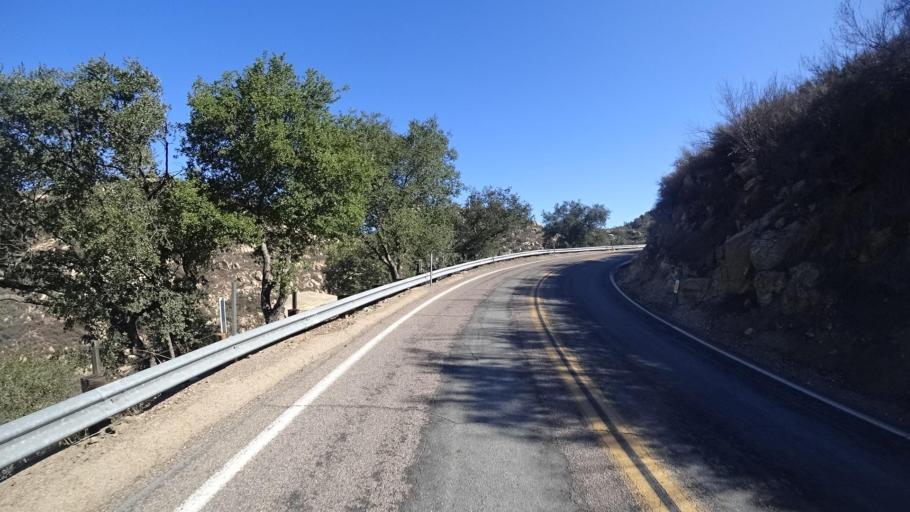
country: US
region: California
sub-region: San Diego County
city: Jamul
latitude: 32.7112
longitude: -116.7779
